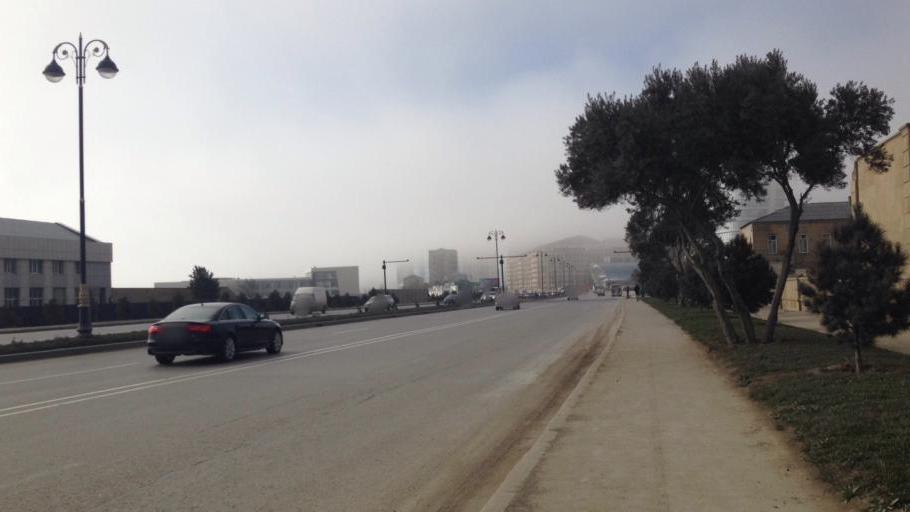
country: AZ
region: Baki
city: Baku
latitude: 40.3792
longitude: 49.8874
